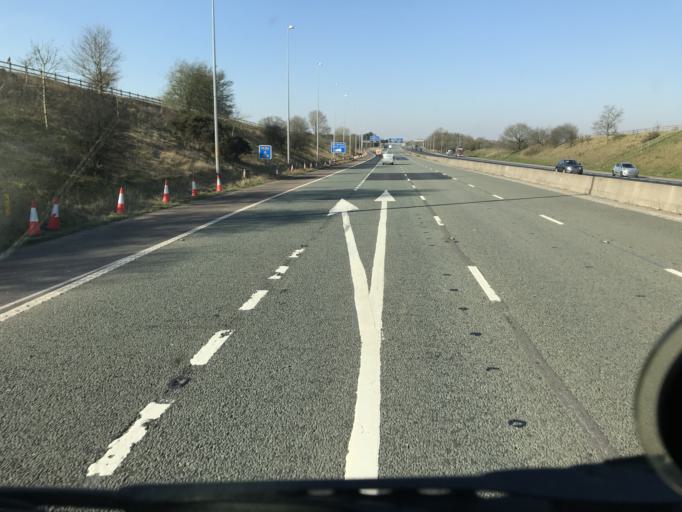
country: GB
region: England
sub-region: Warrington
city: Lymm
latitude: 53.3559
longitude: -2.4900
